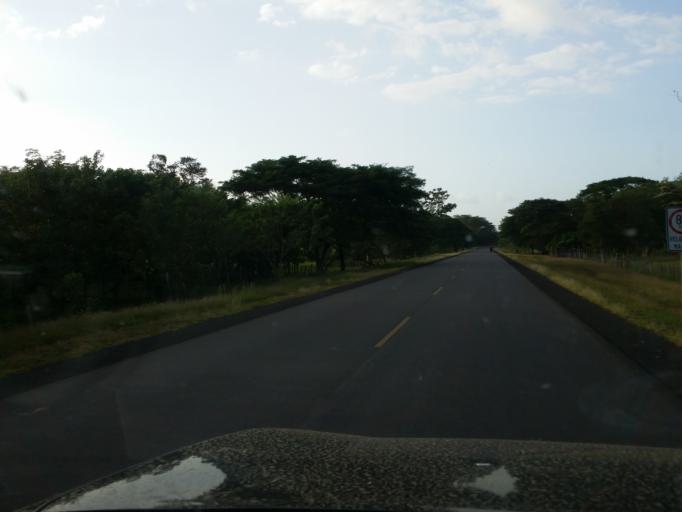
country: NI
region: Rio San Juan
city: San Miguelito
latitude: 11.3658
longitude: -84.7690
